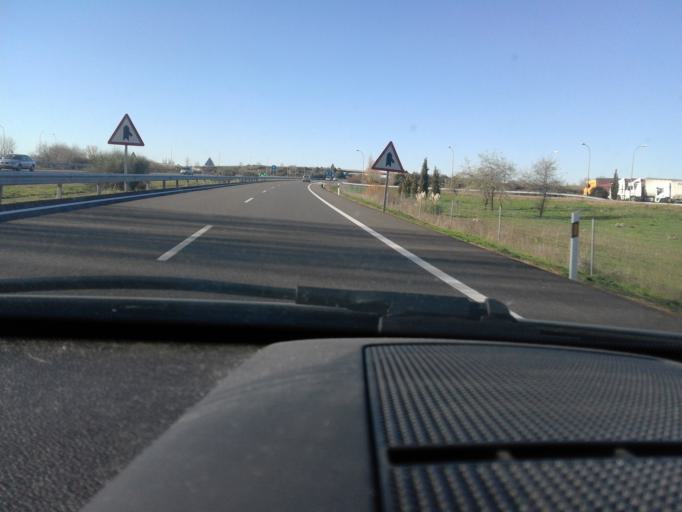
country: ES
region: Castille and Leon
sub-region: Provincia de Leon
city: Sahagun
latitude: 42.3810
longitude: -5.0473
